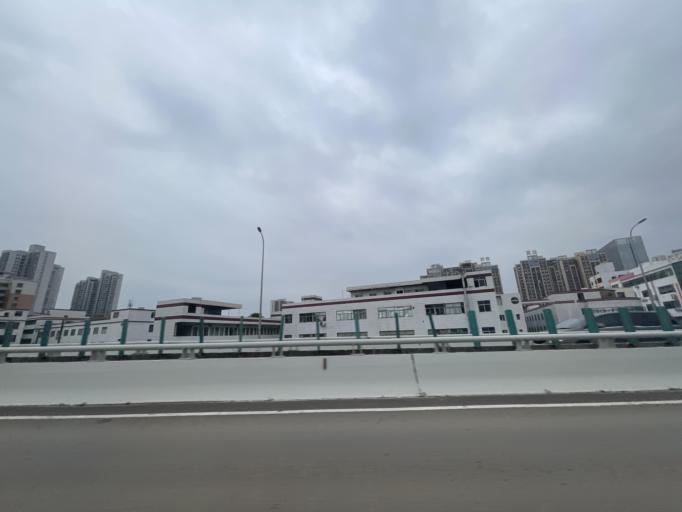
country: CN
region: Guangdong
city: Humen
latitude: 22.8061
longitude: 113.6767
